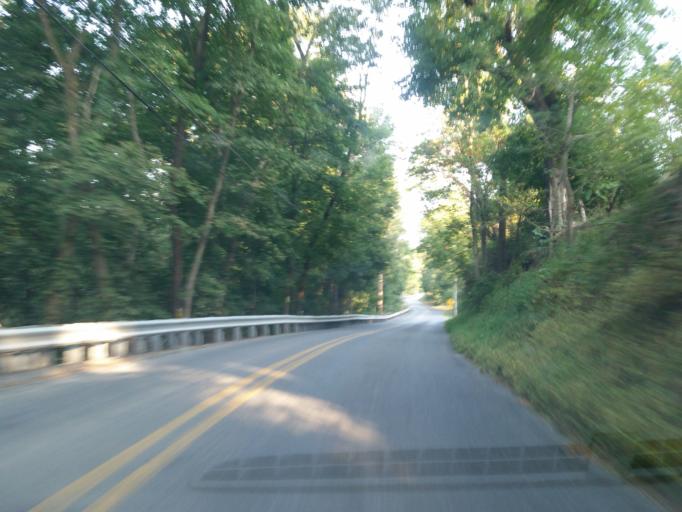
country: US
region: Pennsylvania
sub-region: Lebanon County
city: Annville
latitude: 40.3662
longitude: -76.5225
